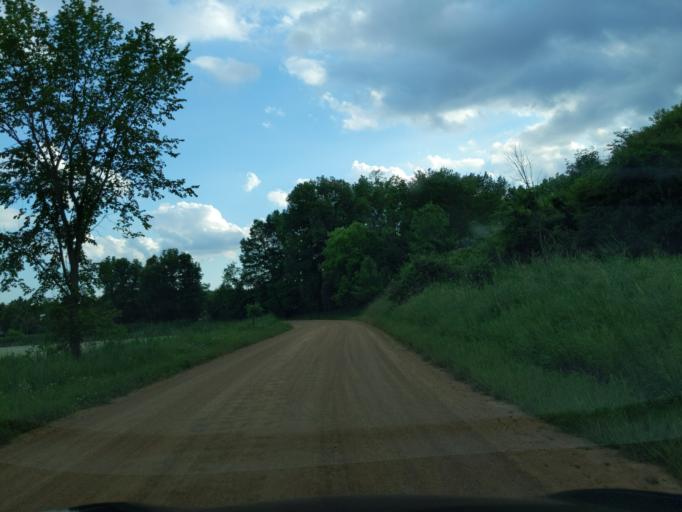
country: US
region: Michigan
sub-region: Shiawassee County
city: Laingsburg
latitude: 42.8324
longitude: -84.3694
